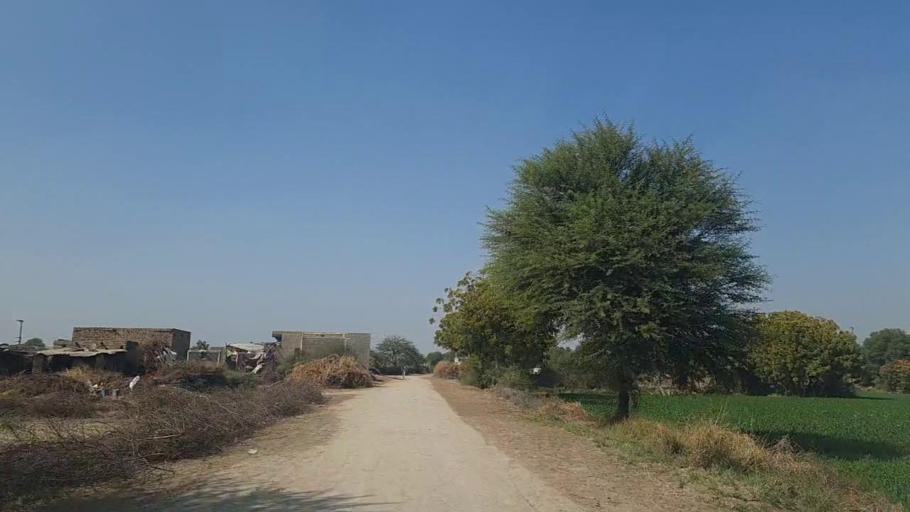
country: PK
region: Sindh
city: Shahpur Chakar
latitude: 26.1805
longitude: 68.5656
